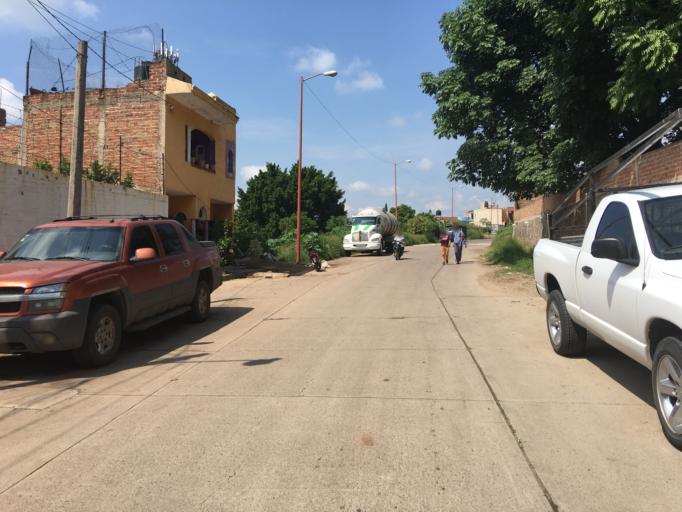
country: MX
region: Jalisco
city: Atotonilco el Alto
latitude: 20.5532
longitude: -102.5110
